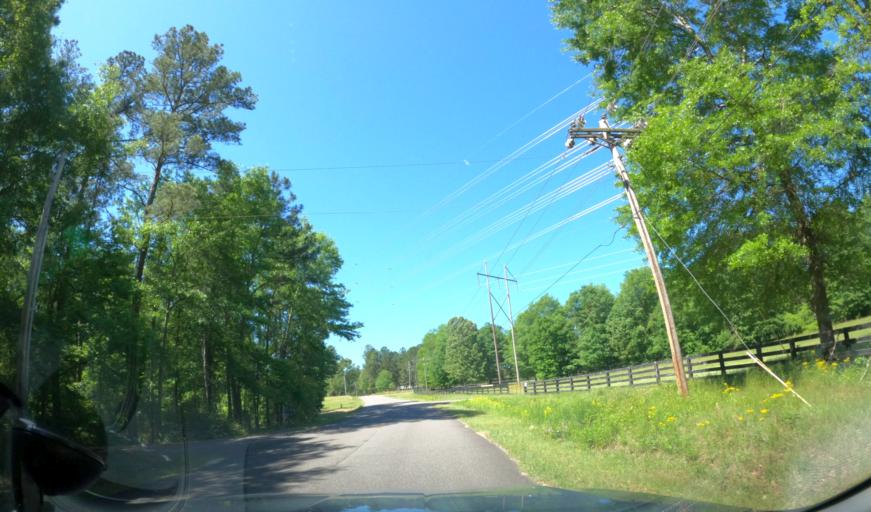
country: US
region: South Carolina
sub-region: Aiken County
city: Langley
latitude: 33.4450
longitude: -81.8080
